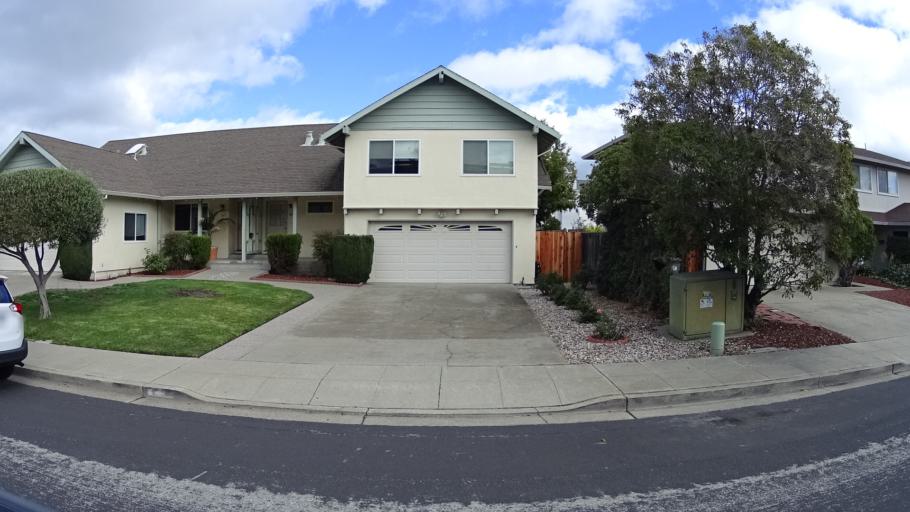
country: US
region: California
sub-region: San Mateo County
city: Foster City
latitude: 37.5617
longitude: -122.2663
